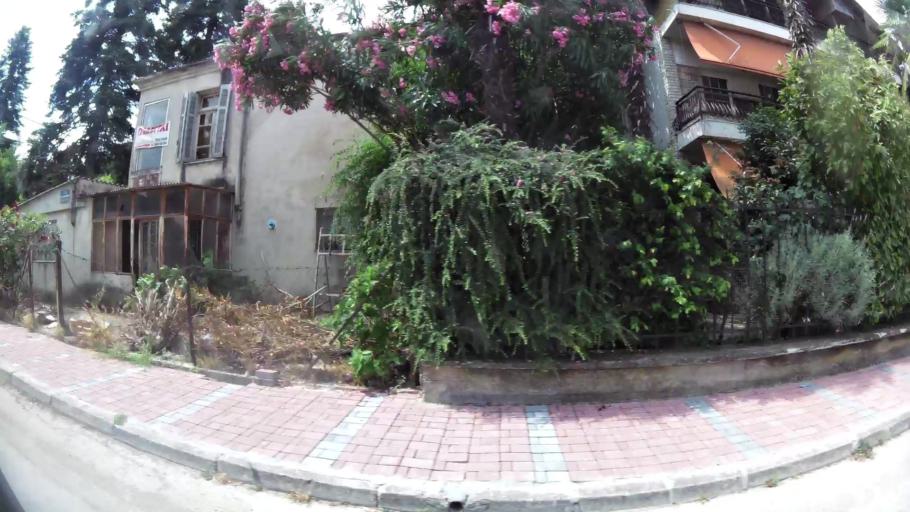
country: GR
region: Central Macedonia
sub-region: Nomos Pierias
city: Katerini
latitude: 40.2777
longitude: 22.5003
